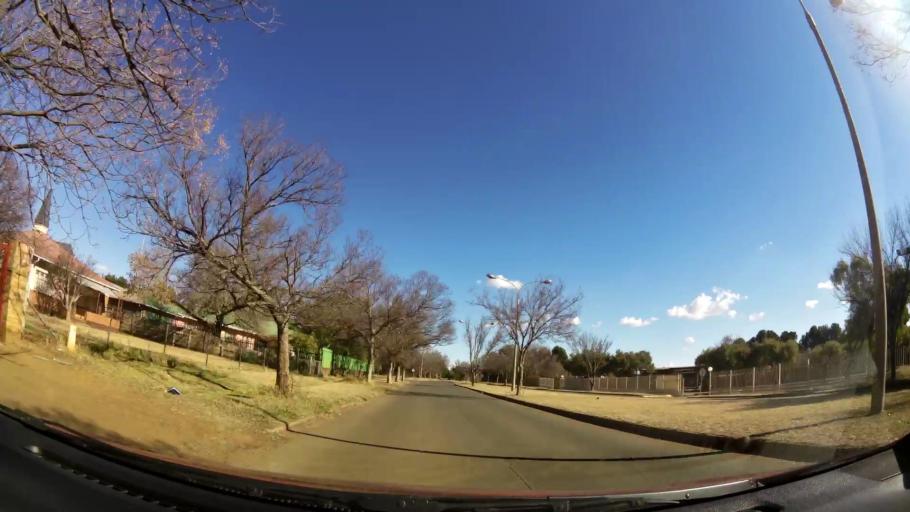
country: ZA
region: Gauteng
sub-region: West Rand District Municipality
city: Carletonville
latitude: -26.3646
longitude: 27.3897
